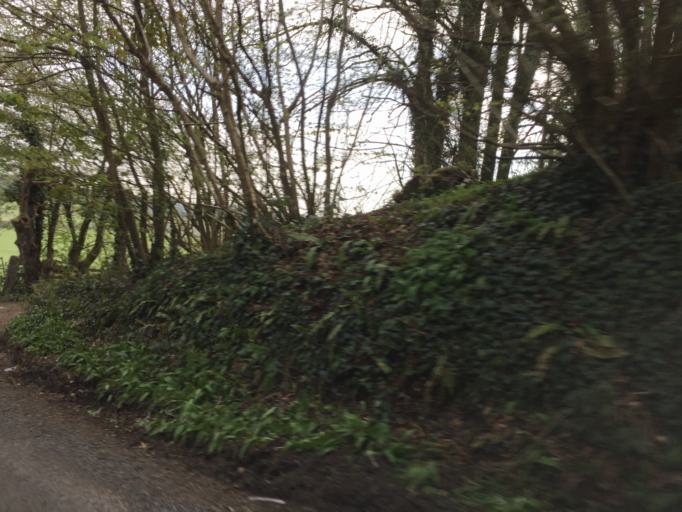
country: GB
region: Wales
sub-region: Cardiff
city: Radyr
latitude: 51.5409
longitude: -3.2361
